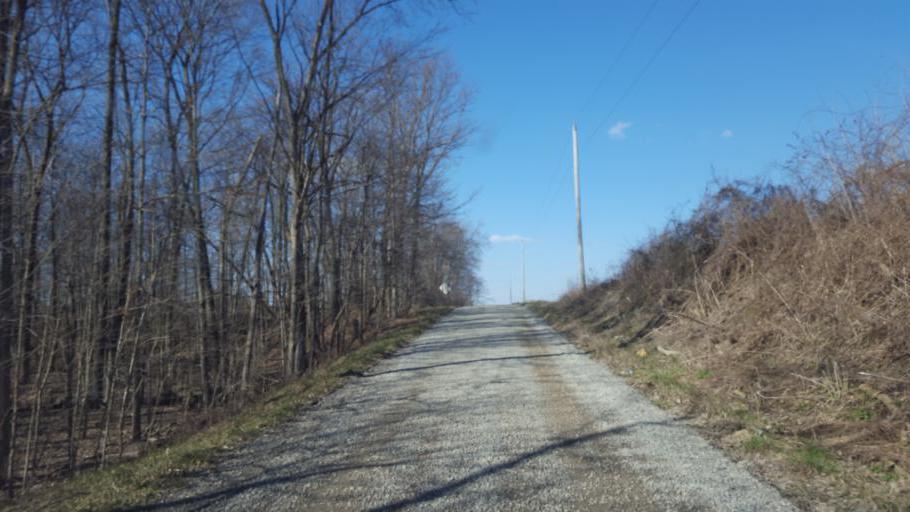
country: US
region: Ohio
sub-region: Morrow County
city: Mount Gilead
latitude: 40.4642
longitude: -82.7450
